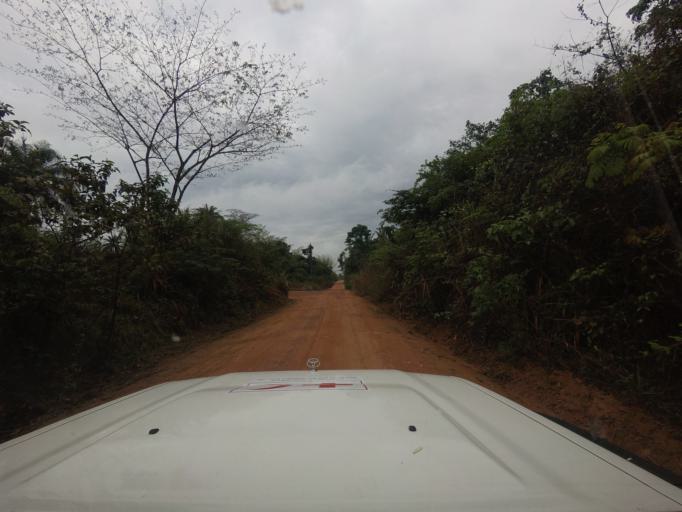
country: SL
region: Eastern Province
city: Buedu
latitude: 8.2851
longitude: -10.1213
